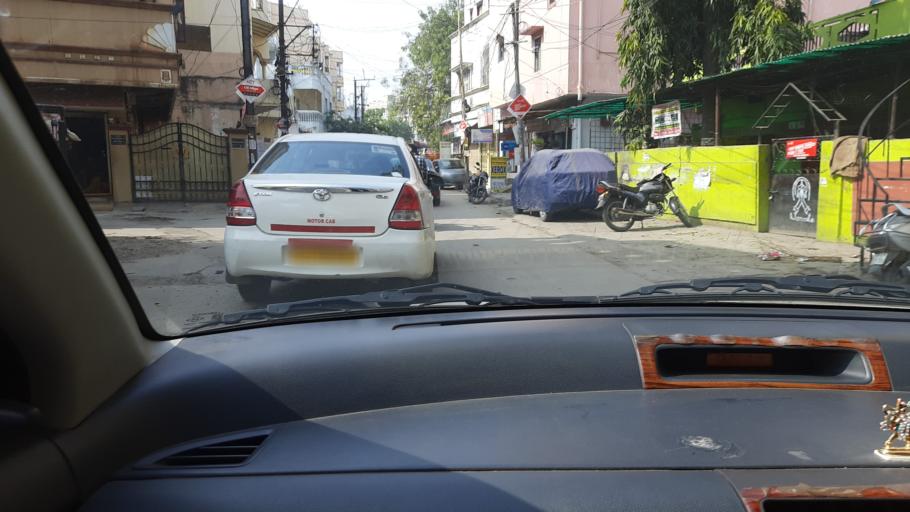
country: IN
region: Telangana
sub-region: Rangareddi
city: Quthbullapur
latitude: 17.4468
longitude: 78.4597
